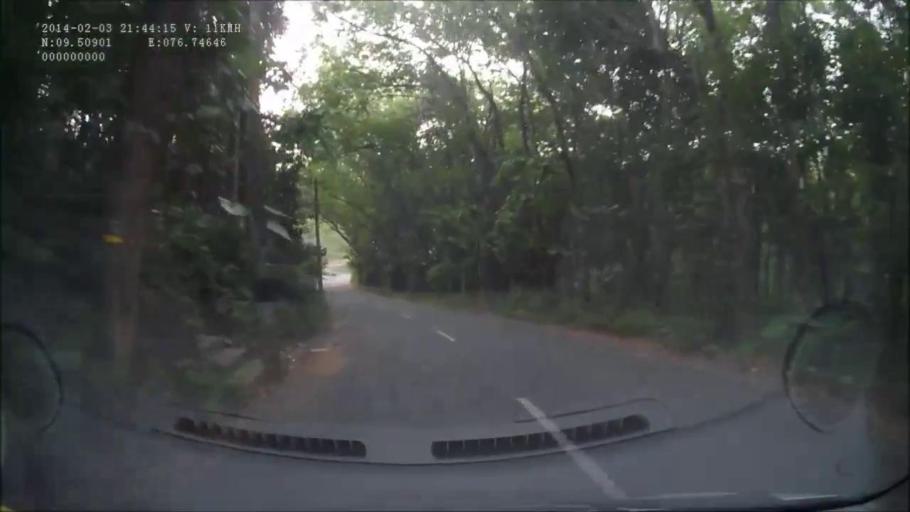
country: IN
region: Kerala
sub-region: Kottayam
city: Erattupetta
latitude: 9.5099
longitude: 76.7449
